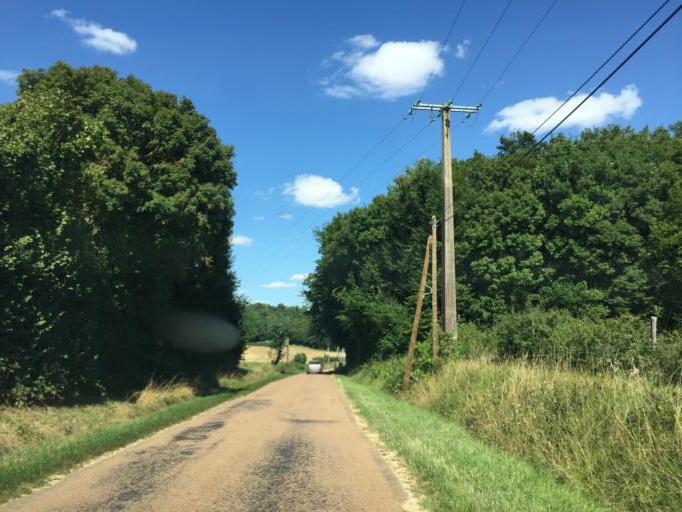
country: FR
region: Bourgogne
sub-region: Departement de l'Yonne
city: Fontenailles
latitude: 47.5630
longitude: 3.3358
